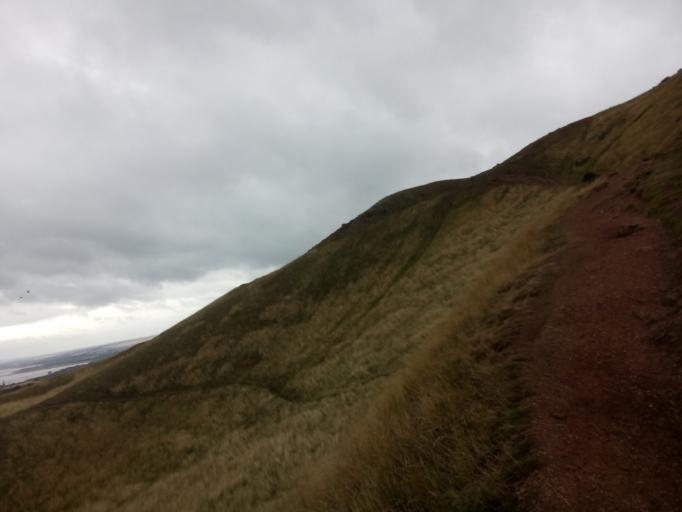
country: GB
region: Scotland
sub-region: West Lothian
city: Seafield
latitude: 55.9456
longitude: -3.1613
